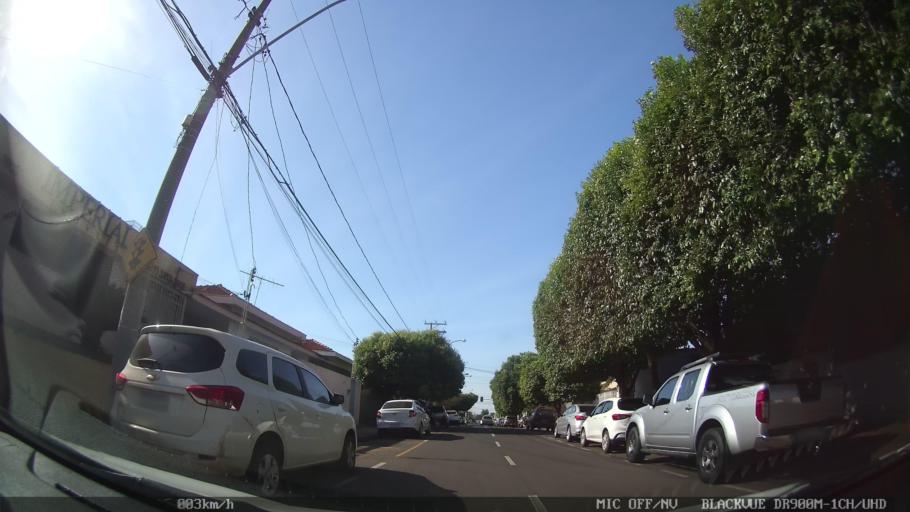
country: BR
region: Sao Paulo
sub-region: Sao Jose Do Rio Preto
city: Sao Jose do Rio Preto
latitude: -20.8062
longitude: -49.3887
